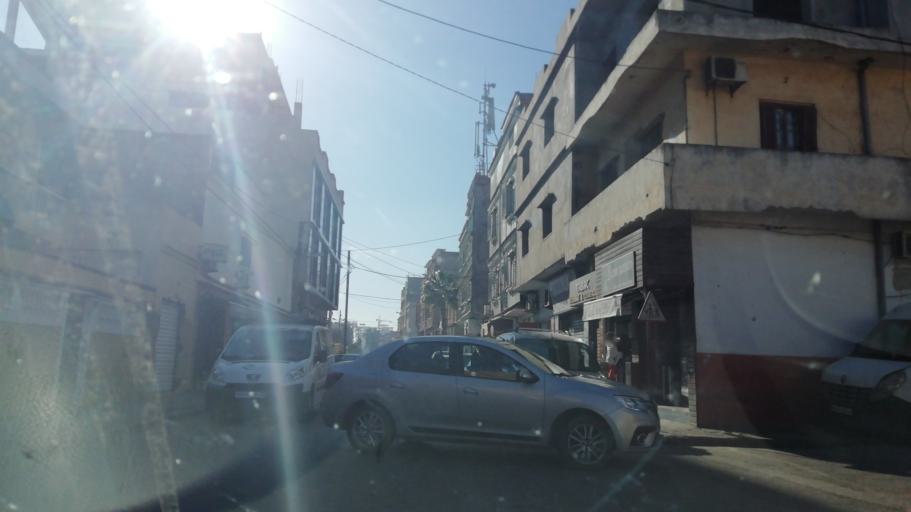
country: DZ
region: Oran
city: Oran
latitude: 35.6736
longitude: -0.6522
